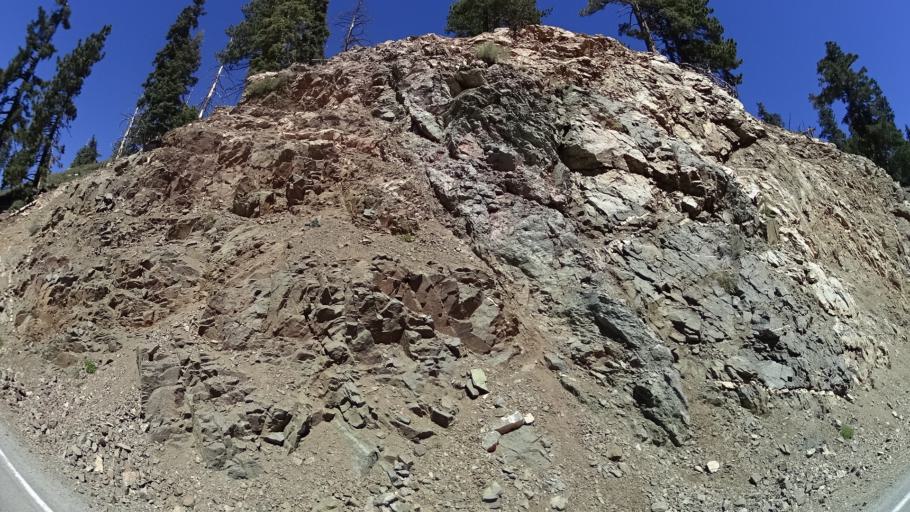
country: US
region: California
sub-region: San Bernardino County
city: Wrightwood
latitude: 34.3485
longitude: -117.8198
